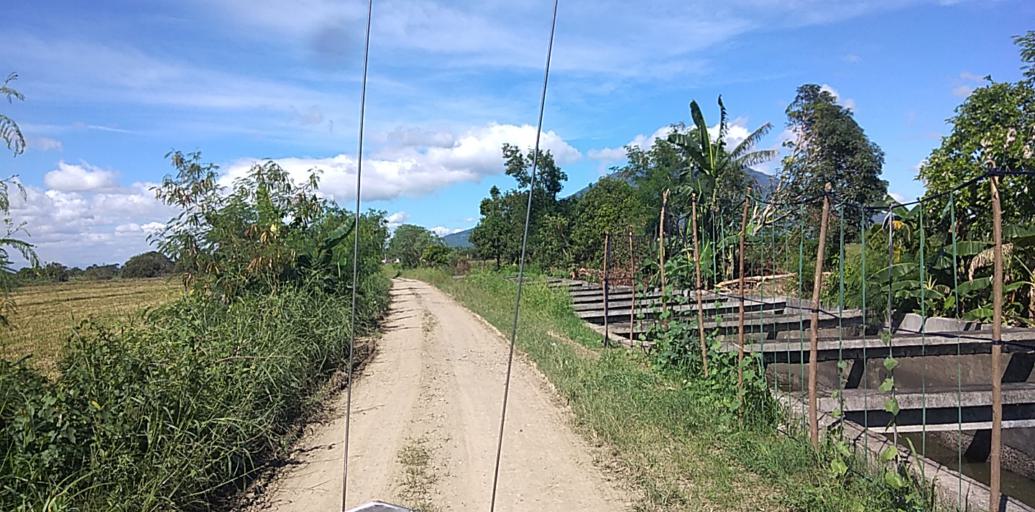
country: PH
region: Central Luzon
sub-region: Province of Pampanga
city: Candating
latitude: 15.1303
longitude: 120.7972
